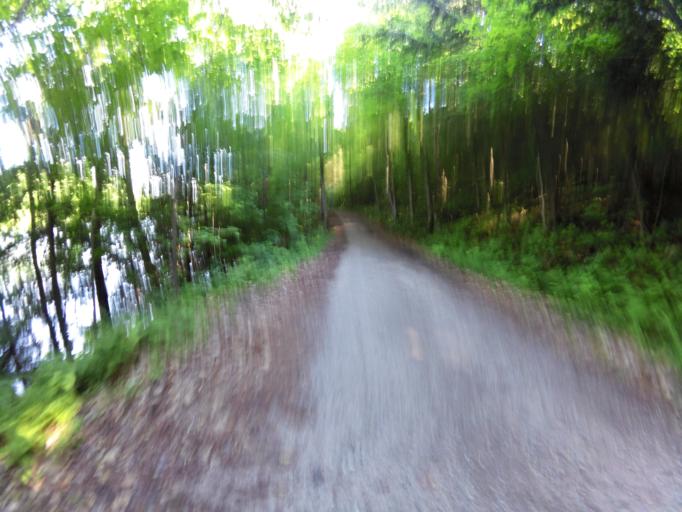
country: CA
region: Quebec
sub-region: Outaouais
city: Wakefield
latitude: 45.5924
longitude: -75.9868
